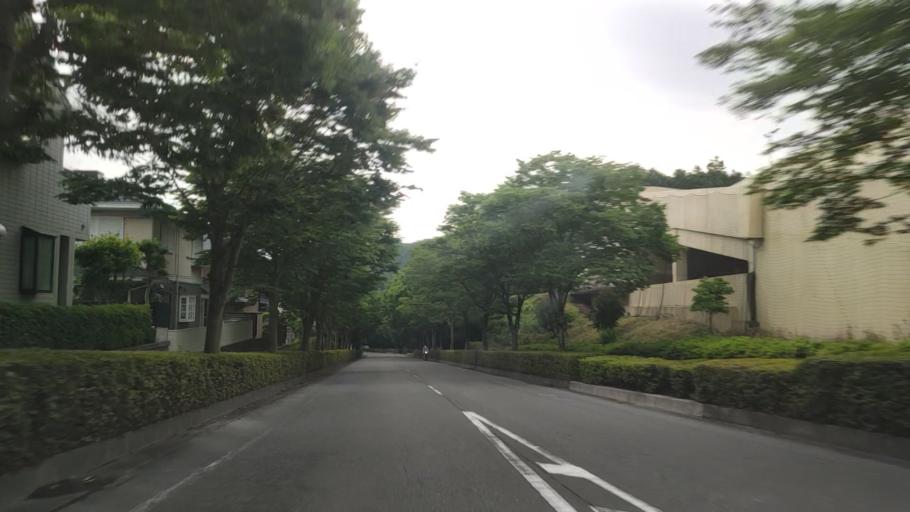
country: JP
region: Saitama
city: Hanno
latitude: 35.8407
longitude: 139.3099
